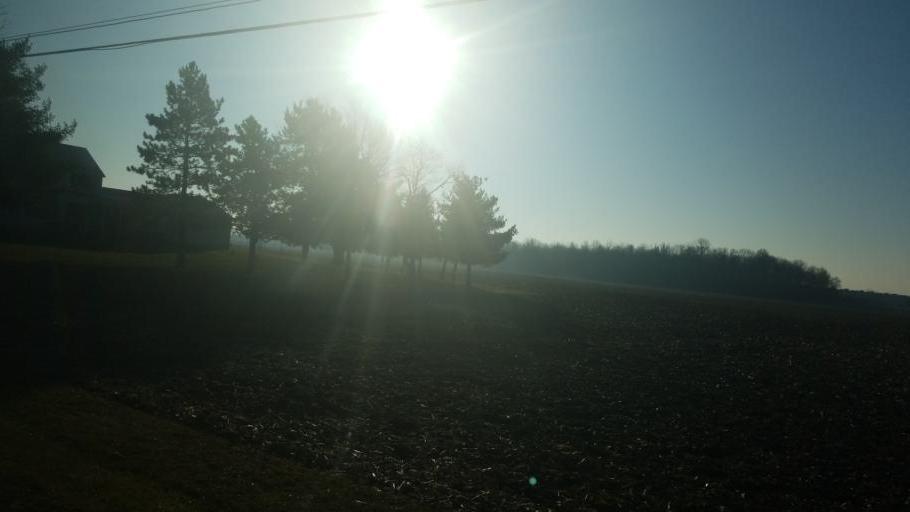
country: US
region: Ohio
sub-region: Crawford County
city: Bucyrus
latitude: 40.8398
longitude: -82.9635
